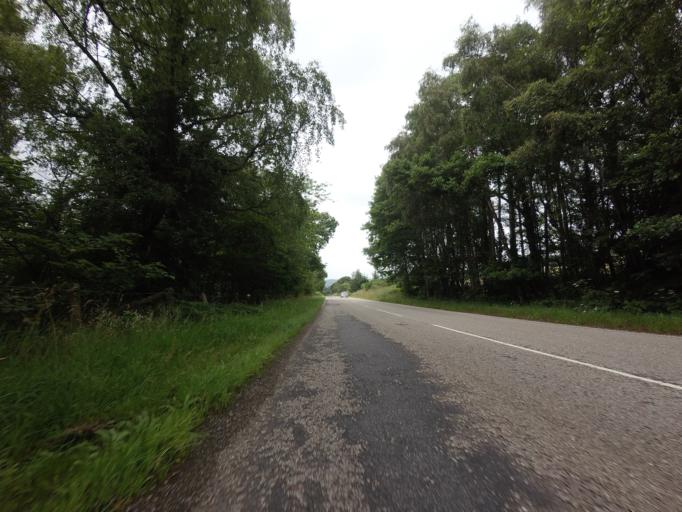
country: GB
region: Scotland
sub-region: Highland
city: Alness
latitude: 57.9086
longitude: -4.3654
